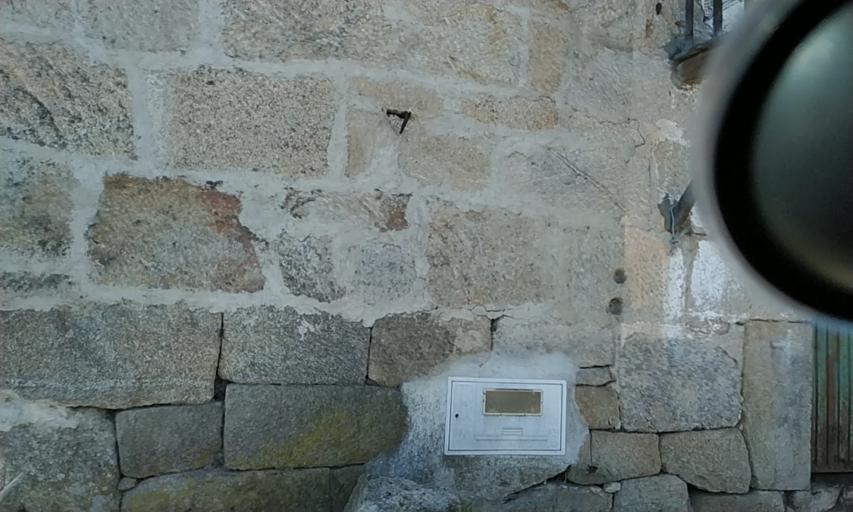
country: PT
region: Vila Real
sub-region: Vila Real
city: Vila Real
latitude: 41.3310
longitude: -7.7528
